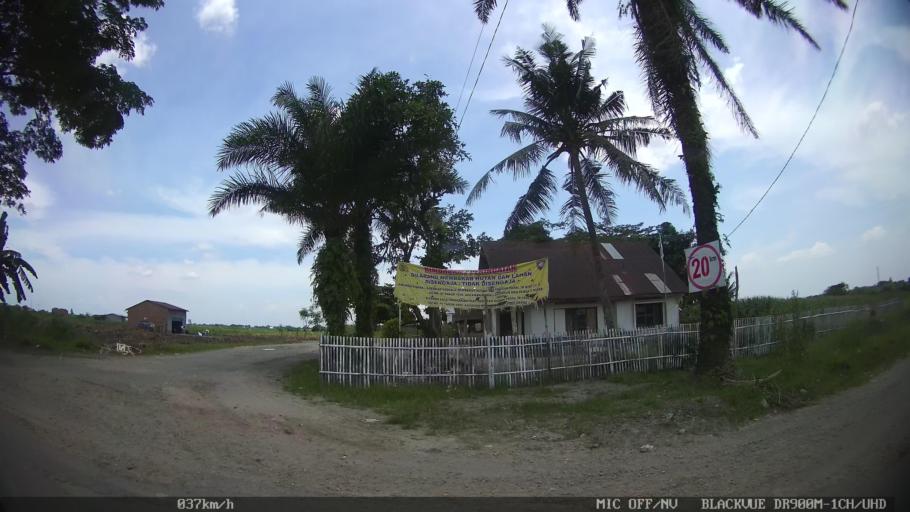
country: ID
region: North Sumatra
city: Binjai
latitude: 3.5913
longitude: 98.5125
